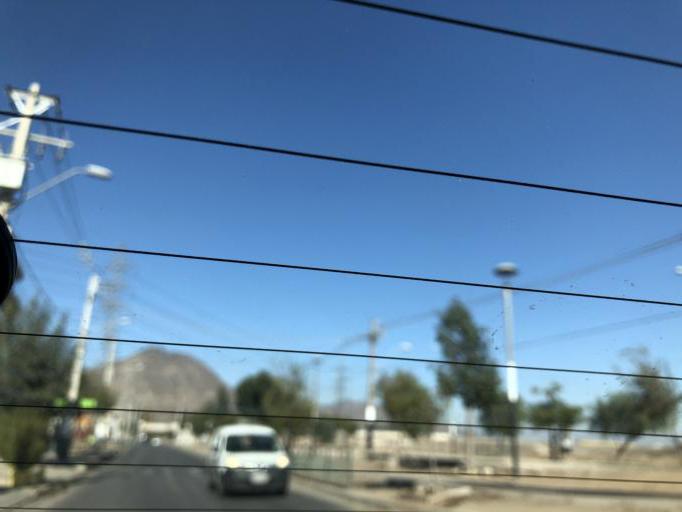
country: CL
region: Santiago Metropolitan
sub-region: Provincia de Santiago
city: La Pintana
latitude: -33.6330
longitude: -70.6297
